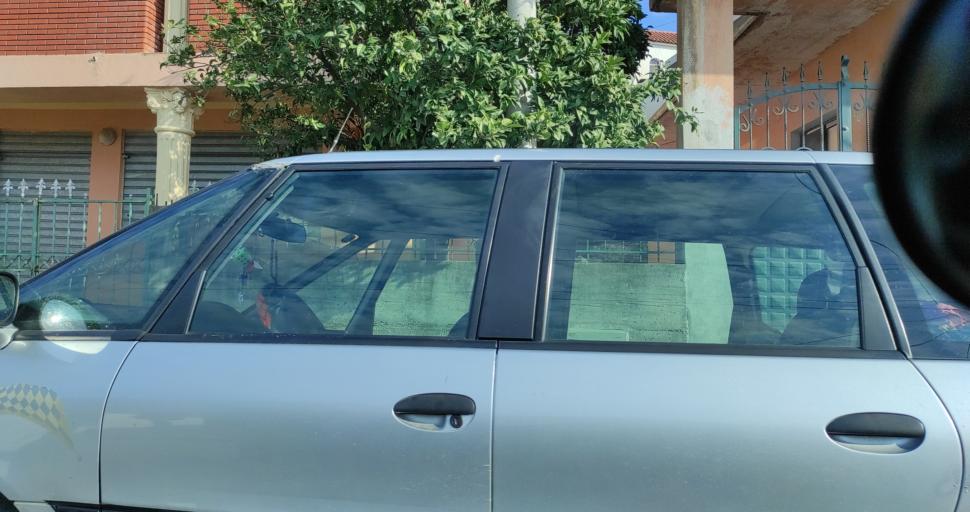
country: AL
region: Lezhe
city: Lezhe
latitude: 41.7866
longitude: 19.6447
